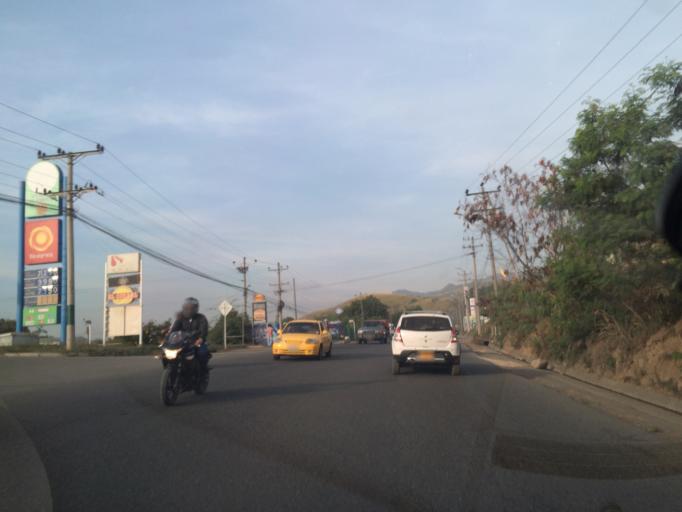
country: CO
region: Valle del Cauca
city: Cali
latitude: 3.5092
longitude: -76.5194
